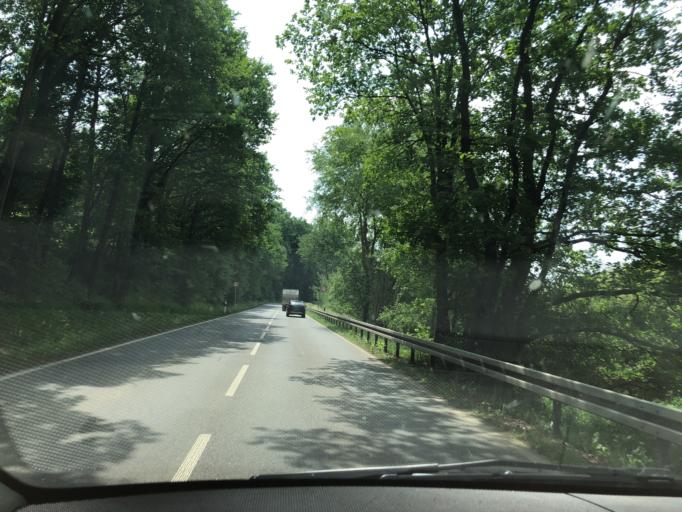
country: DE
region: Hesse
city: Neustadt (Hessen)
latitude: 50.8653
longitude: 9.1268
